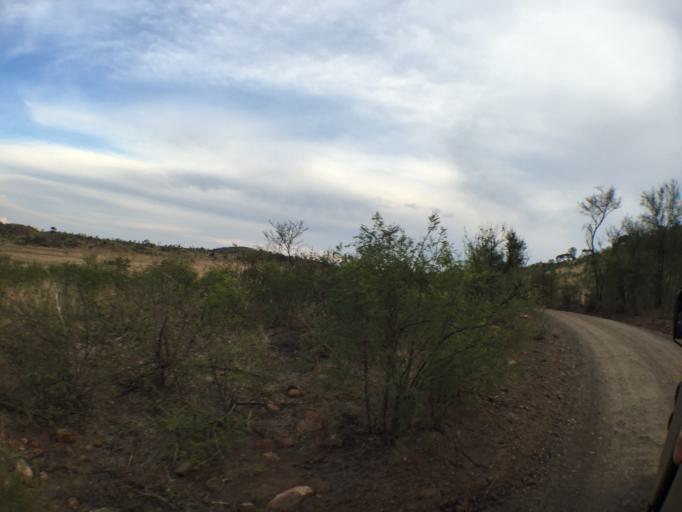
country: ZA
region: North-West
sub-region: Bojanala Platinum District Municipality
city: Mogwase
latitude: -25.2285
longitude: 27.0731
